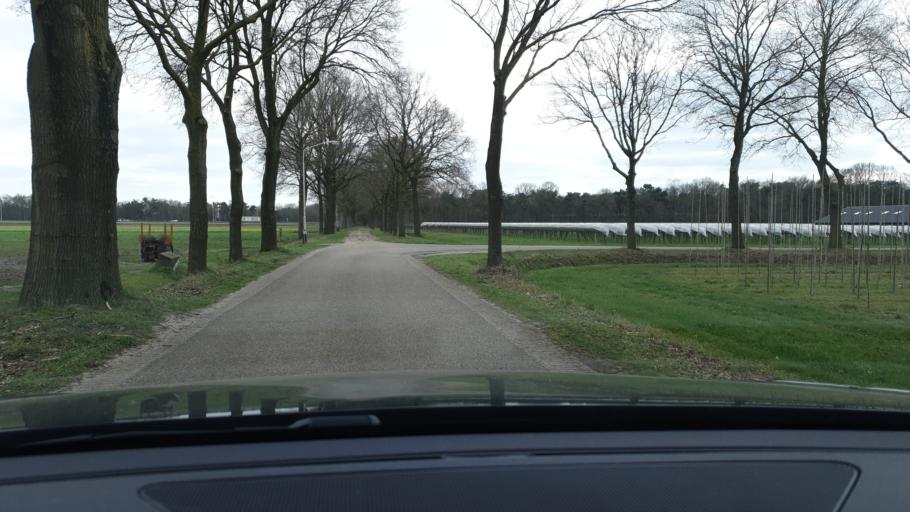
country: NL
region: North Brabant
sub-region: Gemeente Oirschot
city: Oirschot
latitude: 51.4965
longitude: 5.3376
